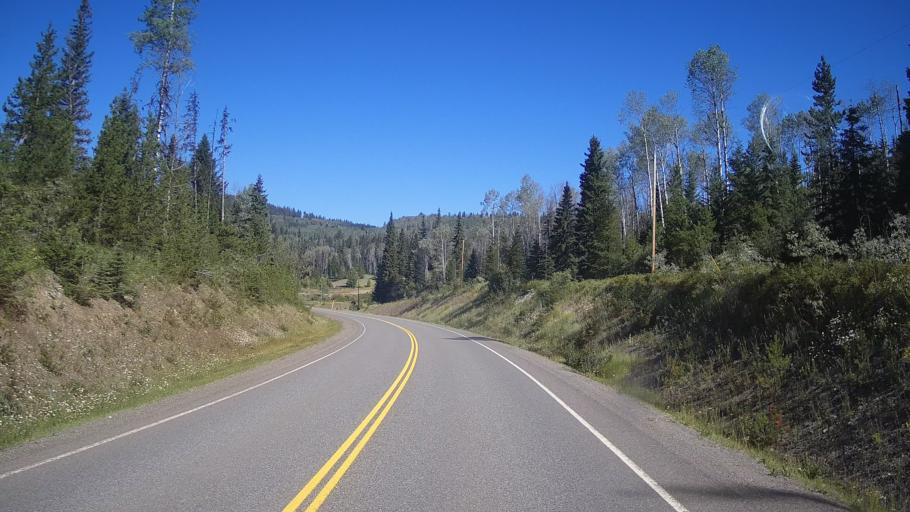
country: CA
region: British Columbia
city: Kamloops
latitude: 51.4886
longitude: -120.5649
